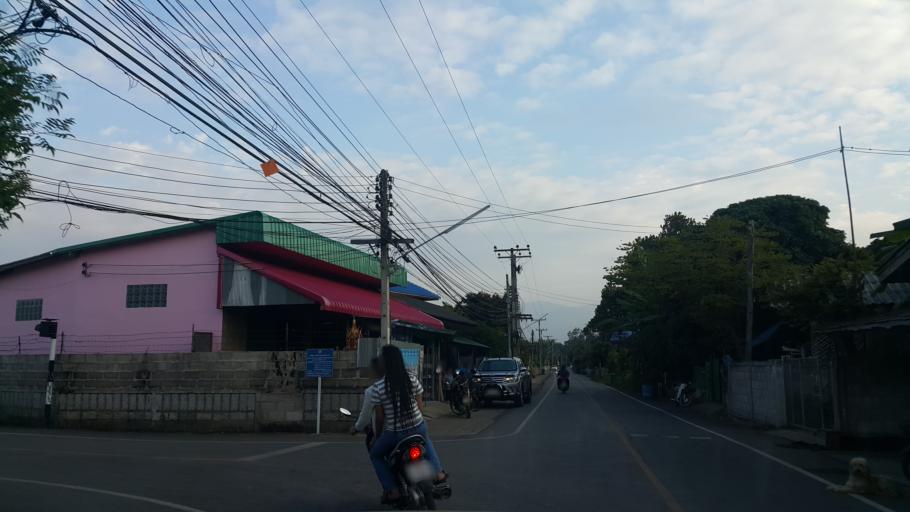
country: TH
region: Lampang
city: Sop Prap
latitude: 17.8902
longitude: 99.3329
